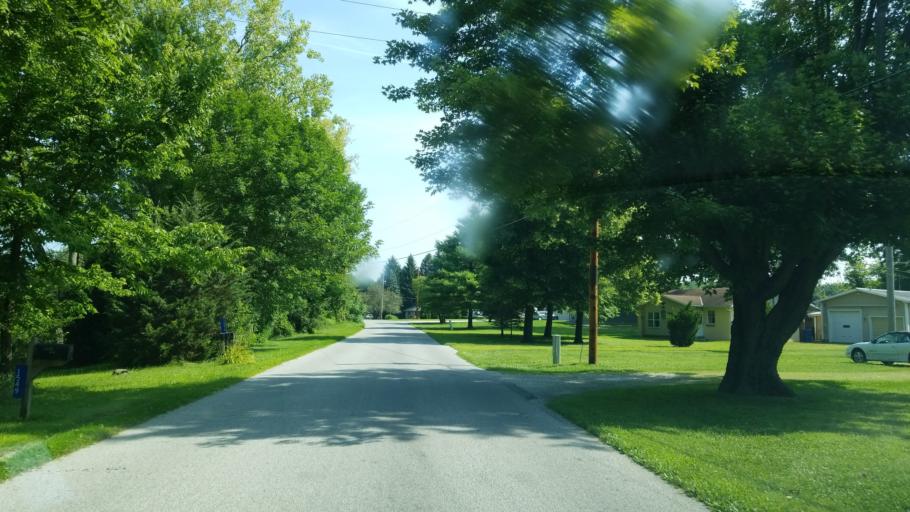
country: US
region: Ohio
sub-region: Seneca County
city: Tiffin
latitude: 41.1459
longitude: -83.1553
